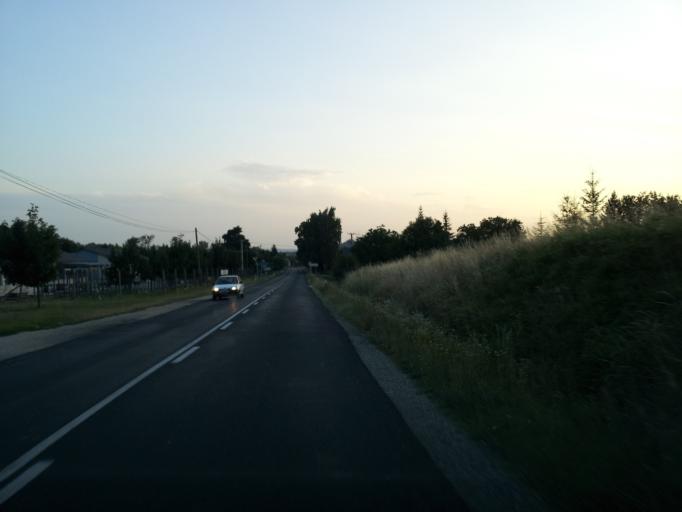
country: HU
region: Veszprem
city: Revfueloep
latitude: 46.9308
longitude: 17.5655
